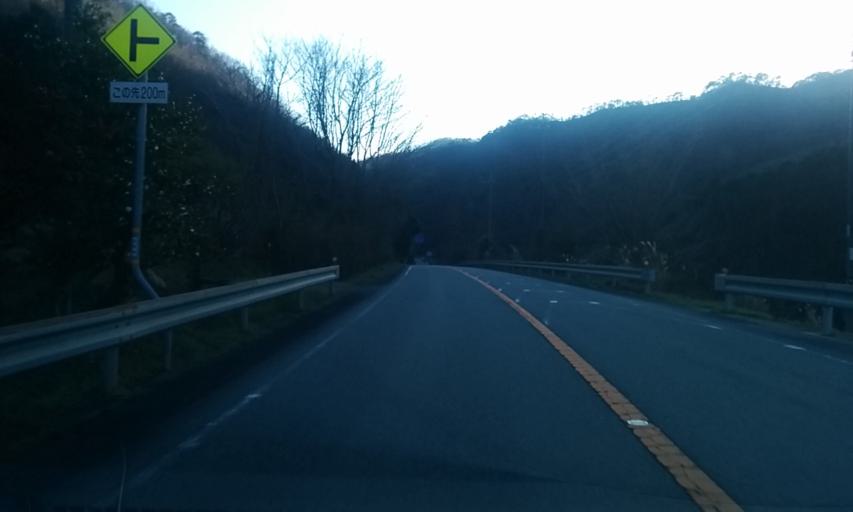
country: JP
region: Hyogo
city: Sasayama
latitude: 35.1387
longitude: 135.3334
